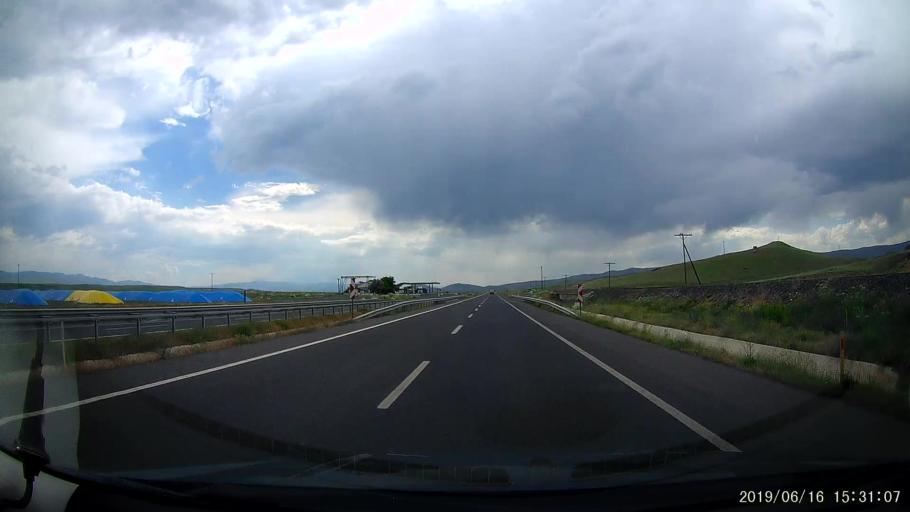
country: TR
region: Erzurum
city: Horasan
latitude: 40.0337
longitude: 42.0872
